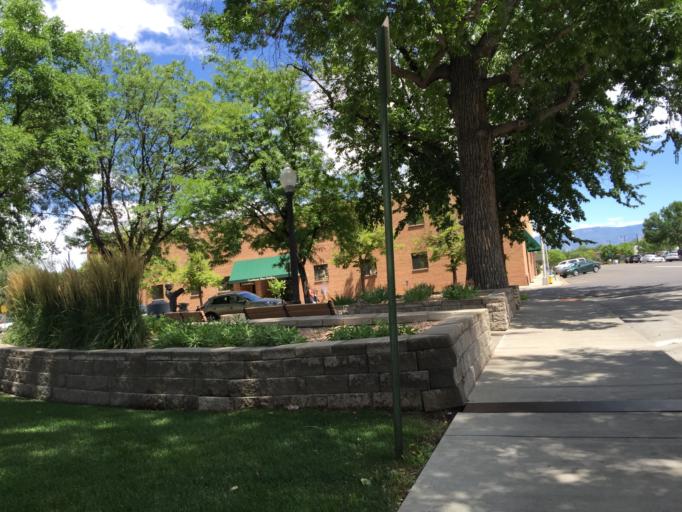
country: US
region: Colorado
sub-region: Mesa County
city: Grand Junction
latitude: 39.0684
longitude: -108.5631
